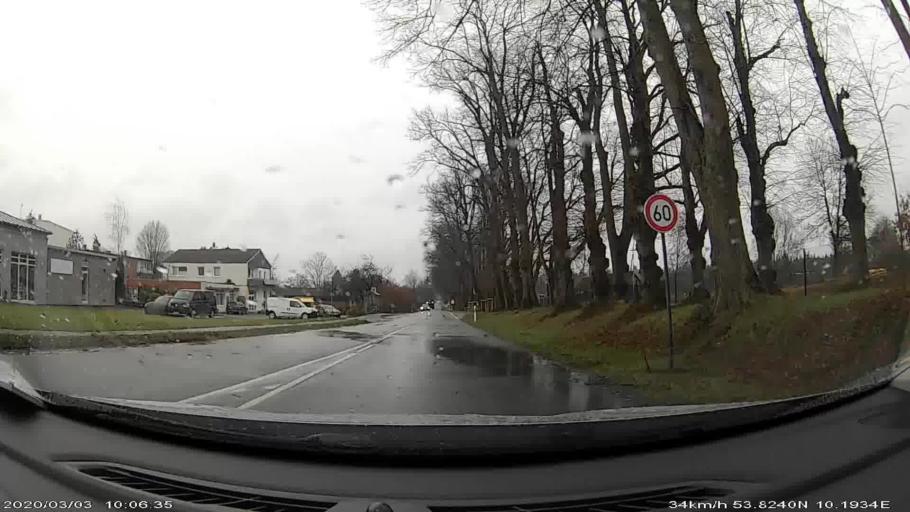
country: DE
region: Schleswig-Holstein
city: Itzstedt
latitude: 53.8222
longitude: 10.1958
